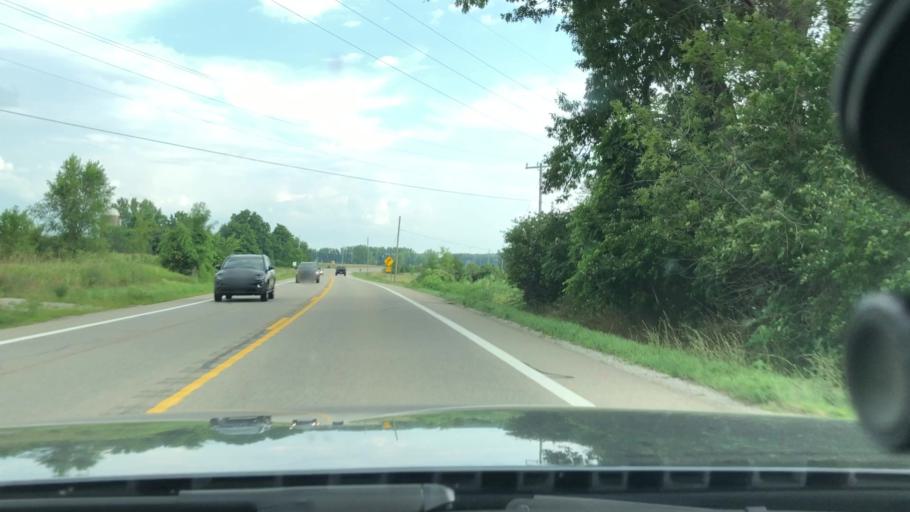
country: US
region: Michigan
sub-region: Washtenaw County
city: Chelsea
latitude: 42.2509
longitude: -84.0338
